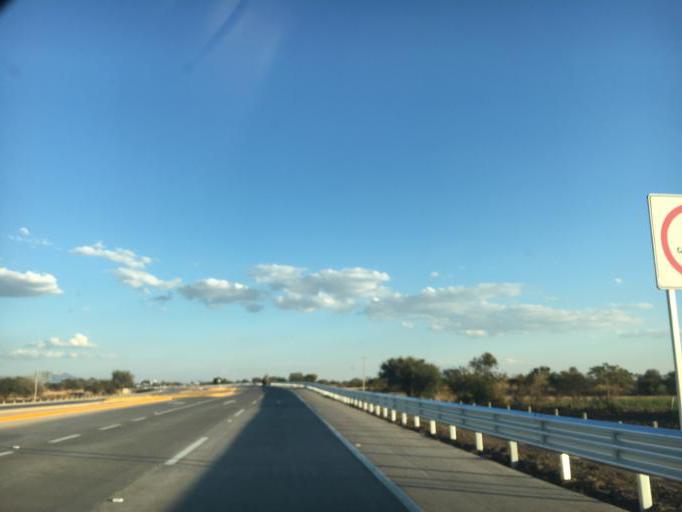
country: MX
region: Guanajuato
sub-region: Leon
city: Fraccionamiento Paraiso Real
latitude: 21.0998
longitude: -101.5733
